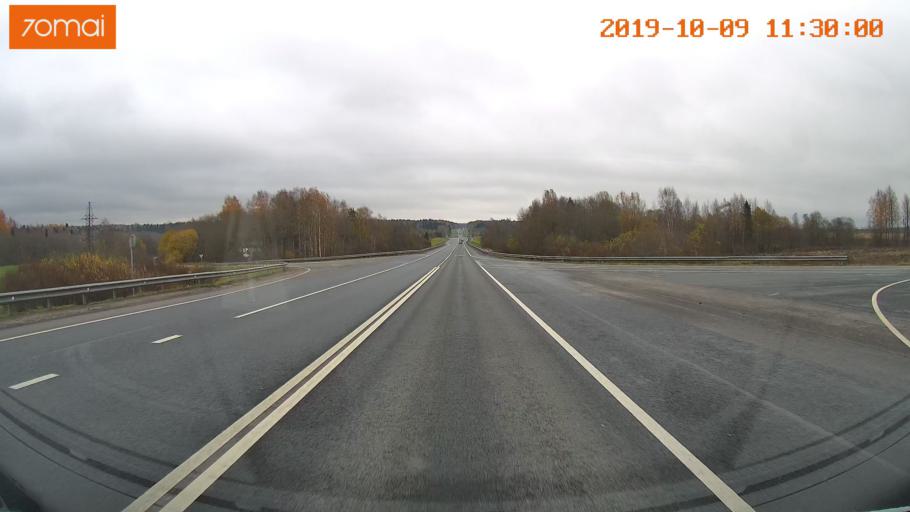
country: RU
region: Vologda
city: Vologda
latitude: 59.0575
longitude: 40.0656
